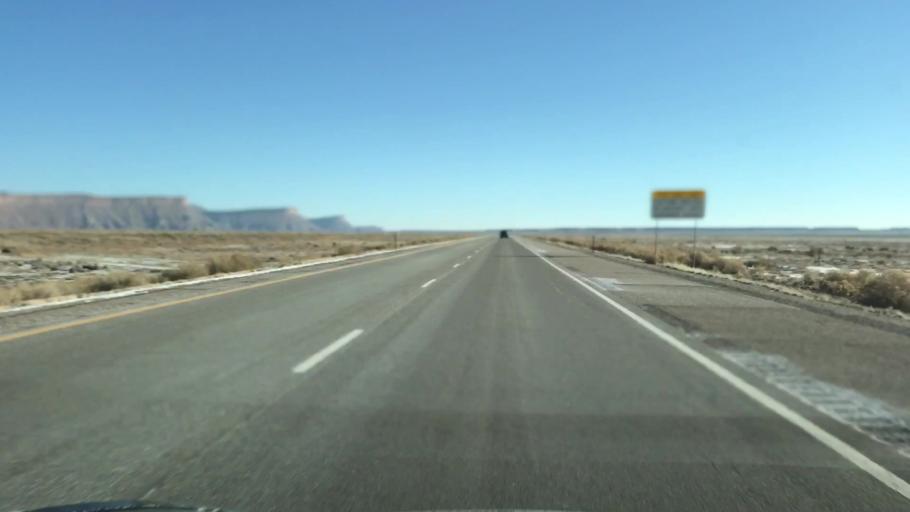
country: US
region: Utah
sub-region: Grand County
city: Moab
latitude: 38.9475
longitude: -109.7865
